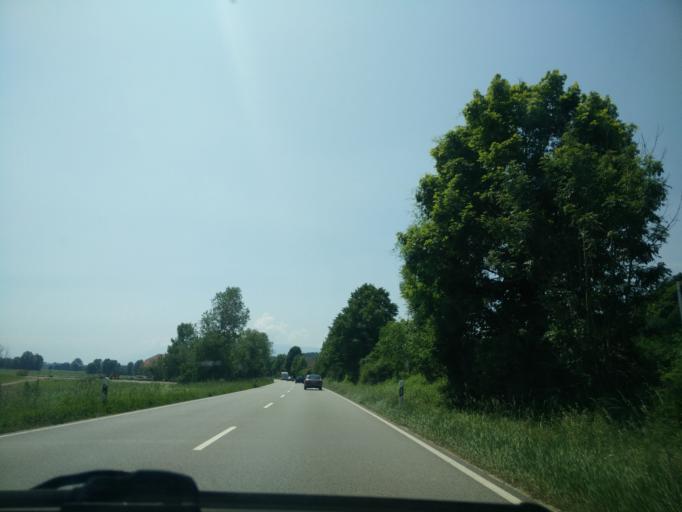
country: DE
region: Bavaria
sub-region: Upper Bavaria
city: Laufen
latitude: 47.9159
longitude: 12.9403
